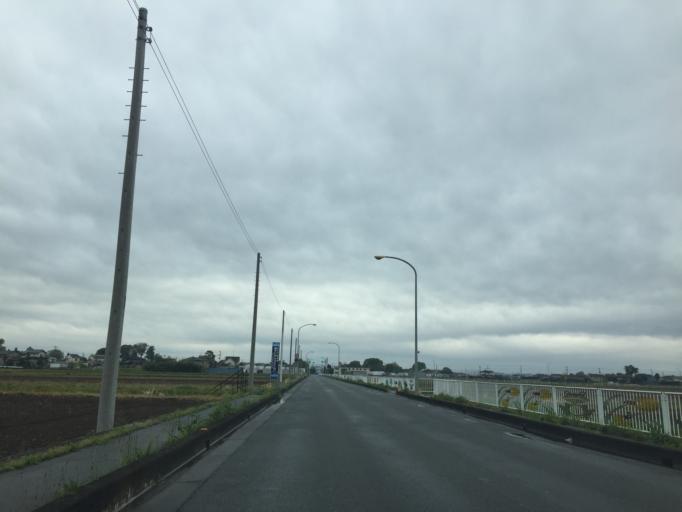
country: JP
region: Saitama
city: Shiki
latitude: 35.8680
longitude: 139.5664
